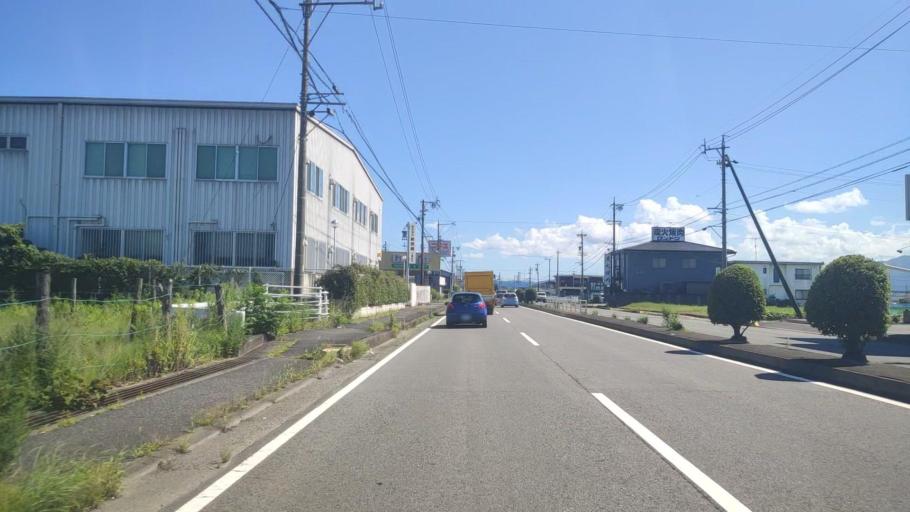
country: JP
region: Mie
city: Hisai-motomachi
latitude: 34.6289
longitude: 136.5167
